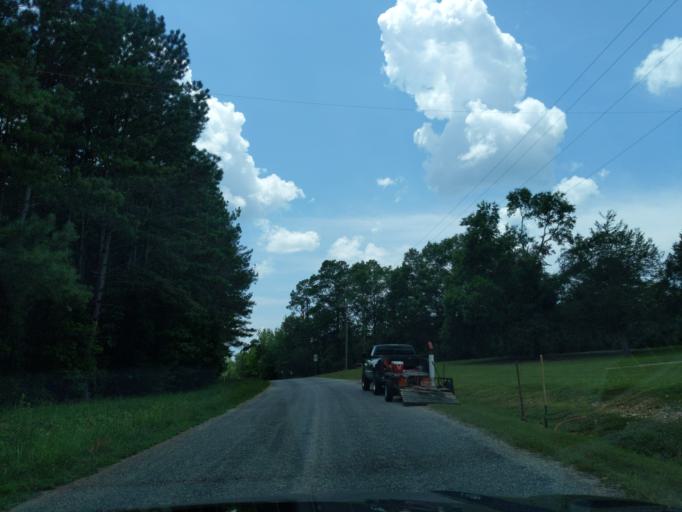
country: US
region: South Carolina
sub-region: Greenwood County
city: Ninety Six
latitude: 34.0358
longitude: -82.0417
